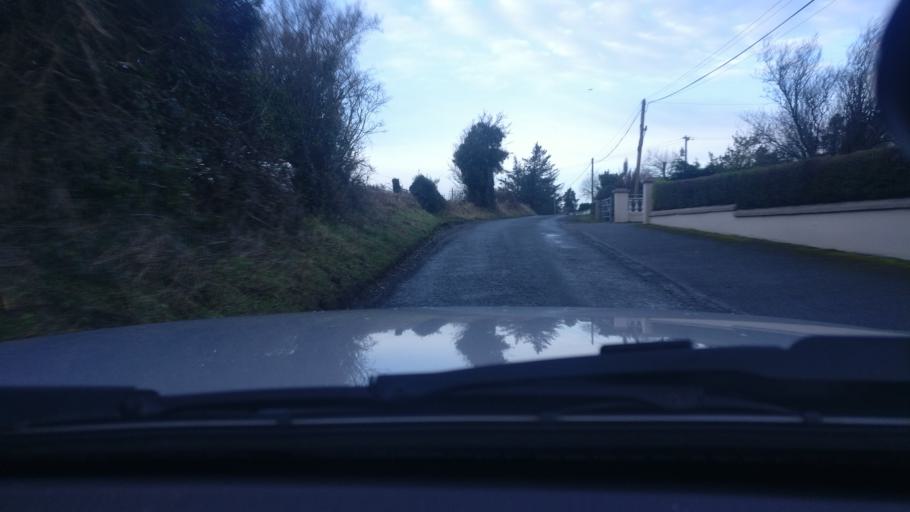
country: IE
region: Connaught
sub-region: County Galway
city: Loughrea
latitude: 53.1732
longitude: -8.5861
